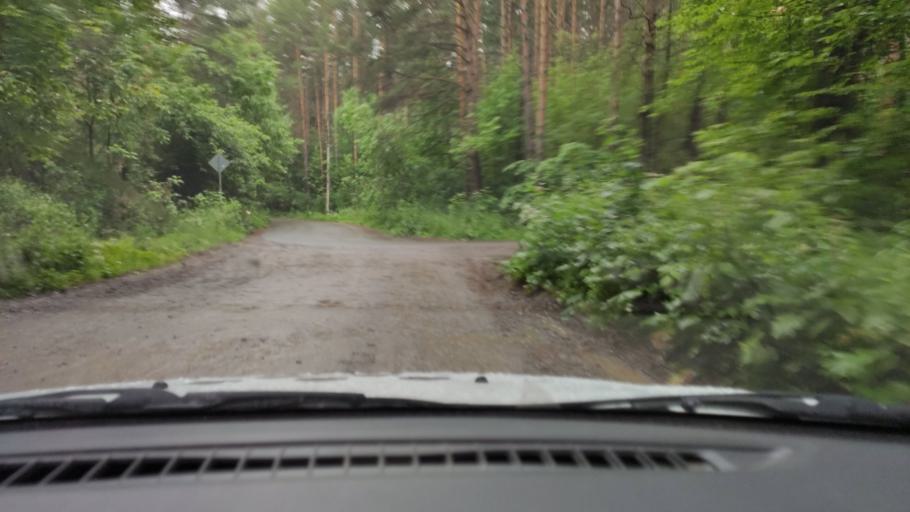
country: RU
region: Udmurtiya
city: Izhevsk
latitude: 56.8851
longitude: 53.1869
